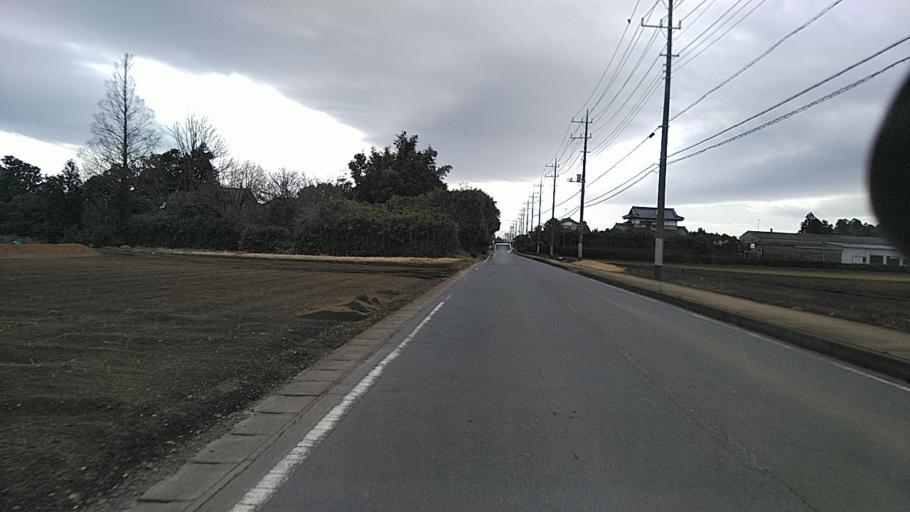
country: JP
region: Chiba
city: Sawara
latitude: 35.8311
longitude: 140.4574
